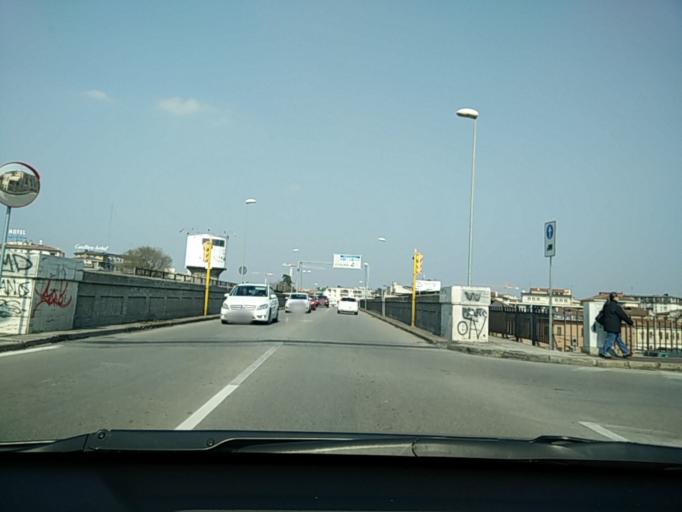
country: IT
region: Veneto
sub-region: Provincia di Treviso
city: Treviso
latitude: 45.6591
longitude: 12.2466
